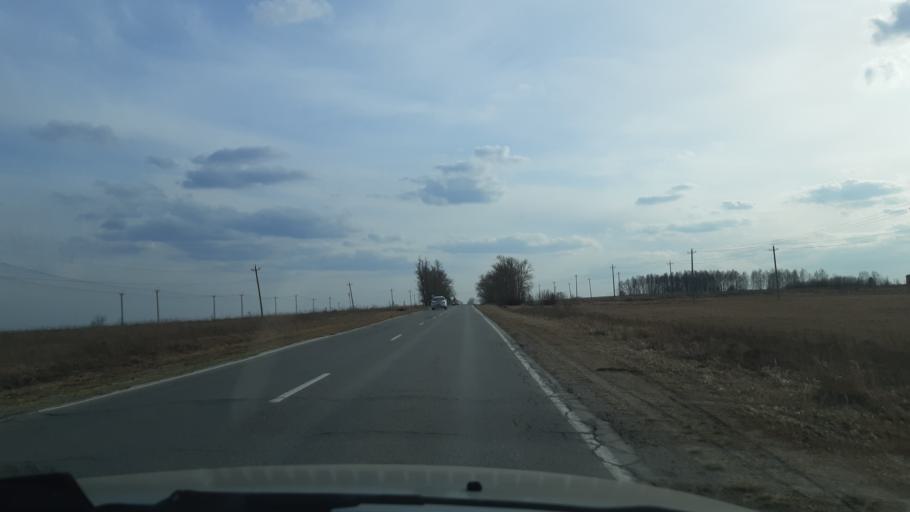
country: RU
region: Vladimir
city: Nikologory
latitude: 56.1676
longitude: 41.9988
